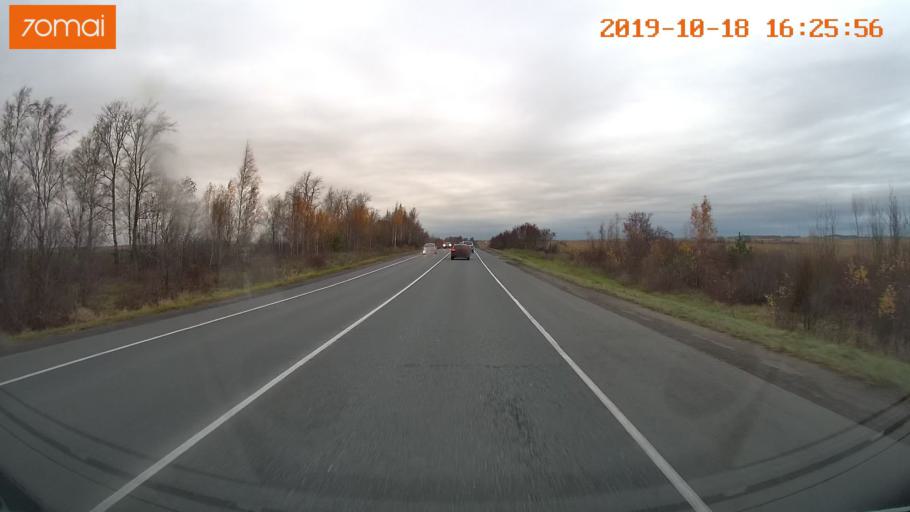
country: RU
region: Vladimir
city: Bogolyubovo
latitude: 56.2815
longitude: 40.4668
